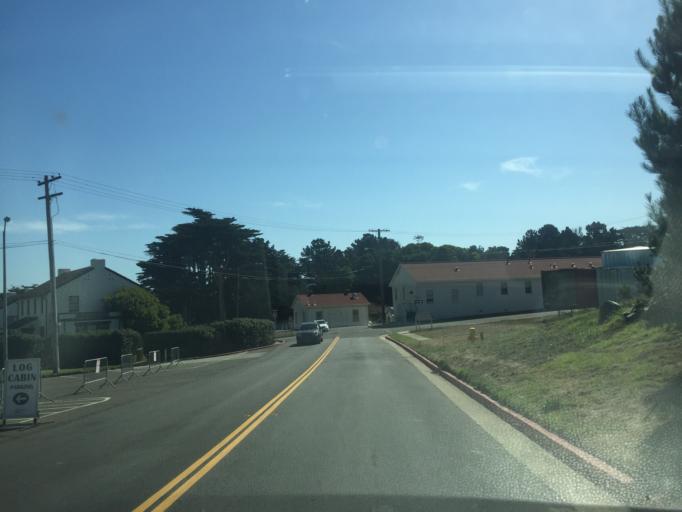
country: US
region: California
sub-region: Marin County
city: Sausalito
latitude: 37.8036
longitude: -122.4739
